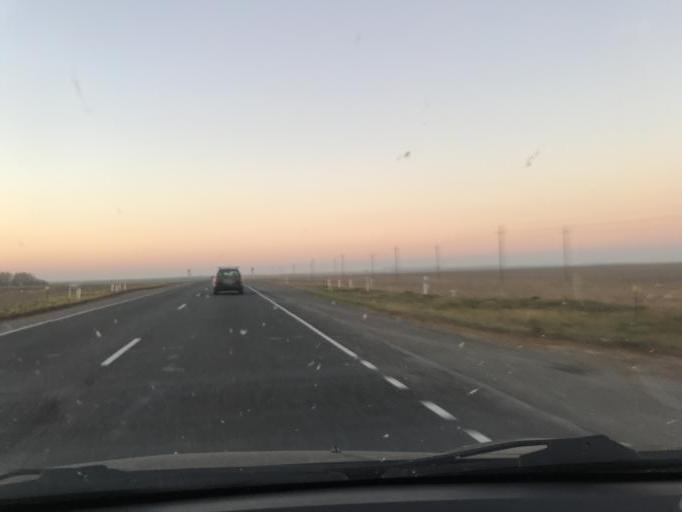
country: BY
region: Gomel
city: Horad Rechytsa
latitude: 52.2720
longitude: 30.4771
